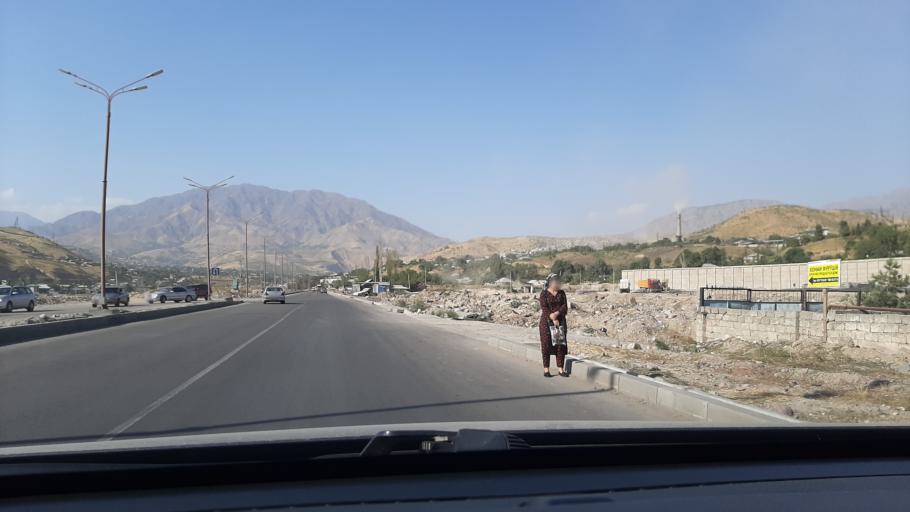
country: TJ
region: Dushanbe
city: Dushanbe
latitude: 38.6353
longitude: 68.7665
